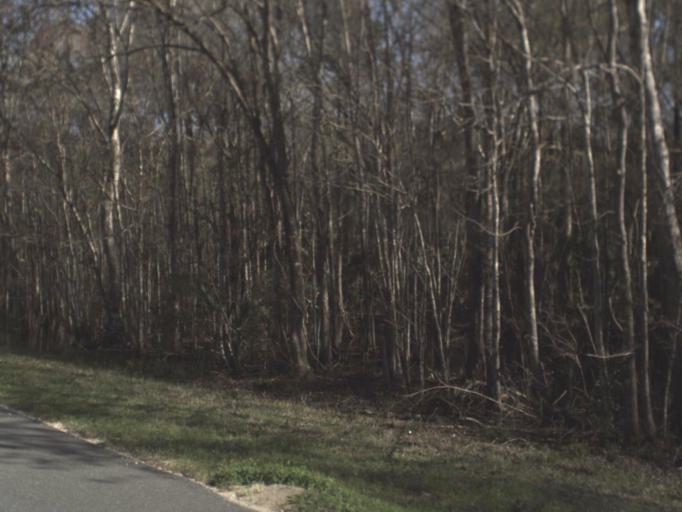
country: US
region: Florida
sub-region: Leon County
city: Woodville
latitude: 30.1772
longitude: -84.0103
